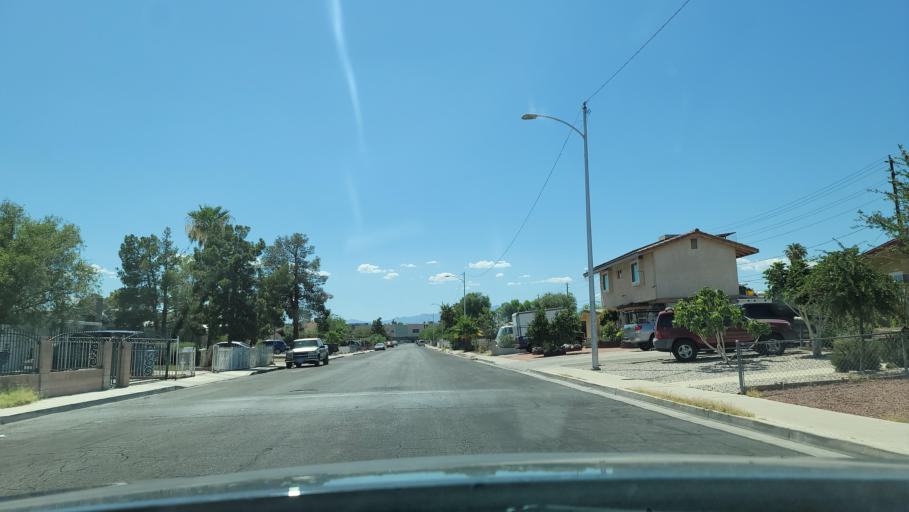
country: US
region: Nevada
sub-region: Clark County
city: Las Vegas
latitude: 36.1771
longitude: -115.1172
